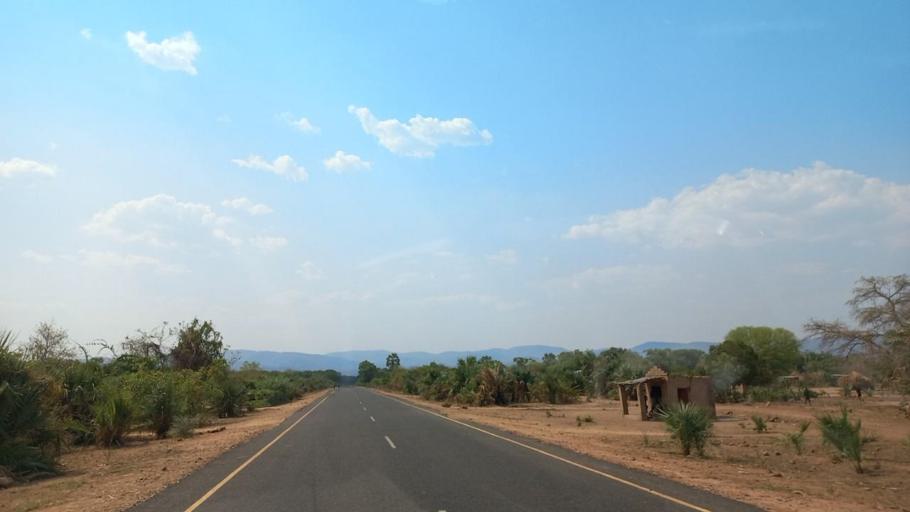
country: ZM
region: Lusaka
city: Luangwa
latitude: -15.1079
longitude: 30.1998
